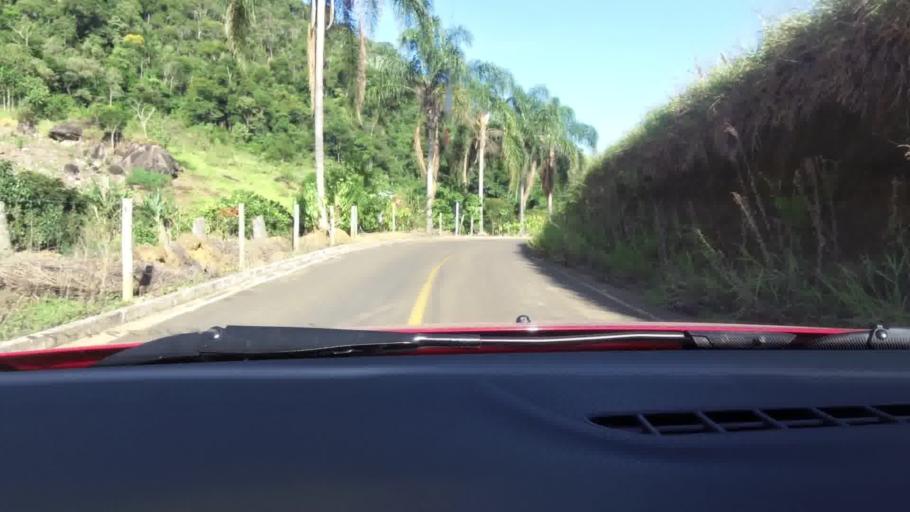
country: BR
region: Espirito Santo
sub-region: Guarapari
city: Guarapari
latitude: -20.5449
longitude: -40.5579
